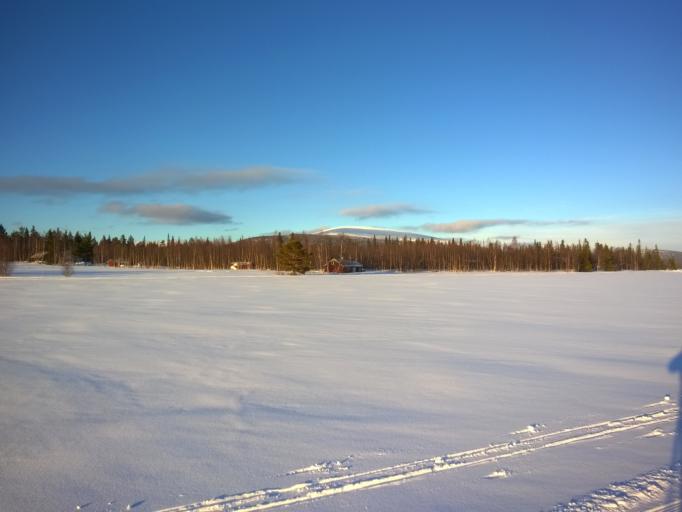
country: FI
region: Lapland
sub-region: Tunturi-Lappi
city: Muonio
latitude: 67.9206
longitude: 24.0524
